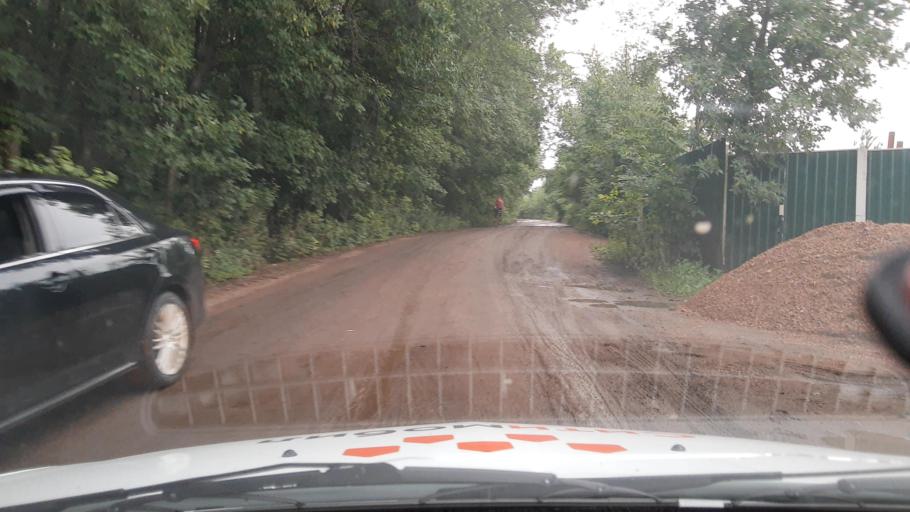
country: RU
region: Bashkortostan
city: Ufa
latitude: 54.5664
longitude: 55.9536
